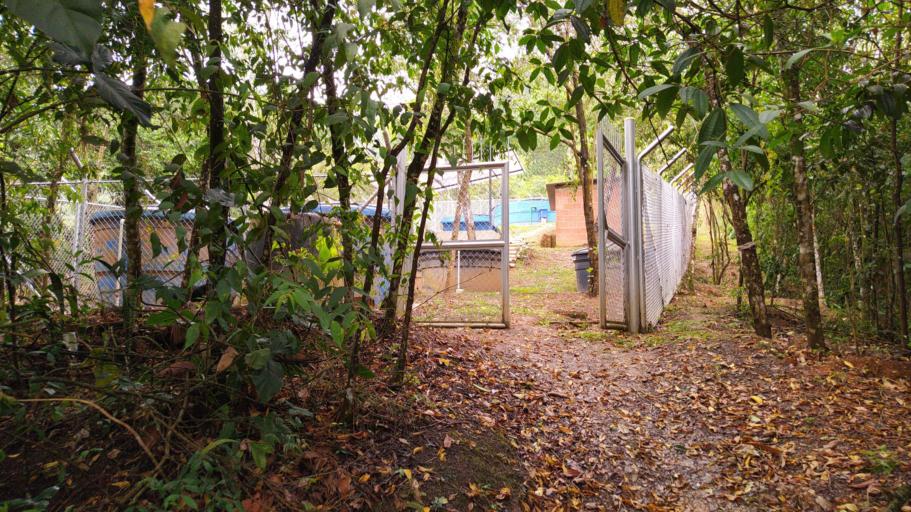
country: CO
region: Valle del Cauca
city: Jamundi
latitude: 3.3165
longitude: -76.5862
